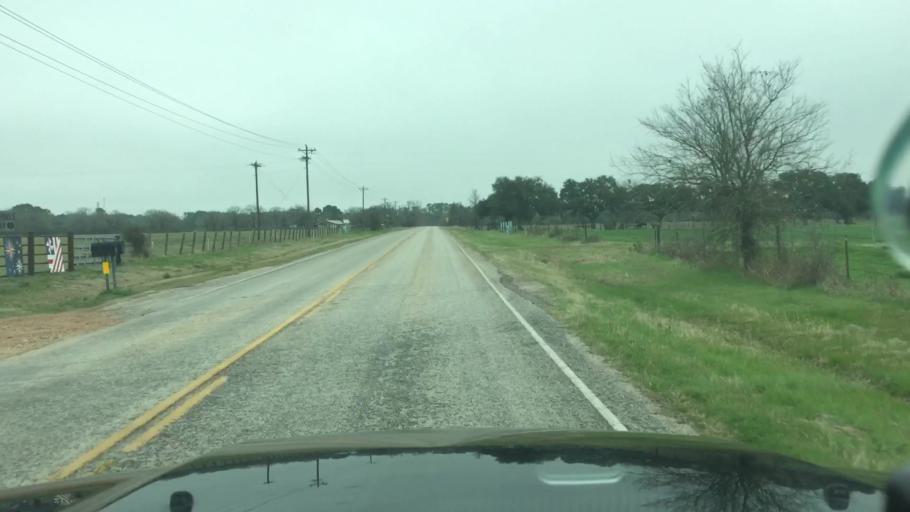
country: US
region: Texas
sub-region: Fayette County
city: La Grange
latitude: 30.0044
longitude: -96.9022
